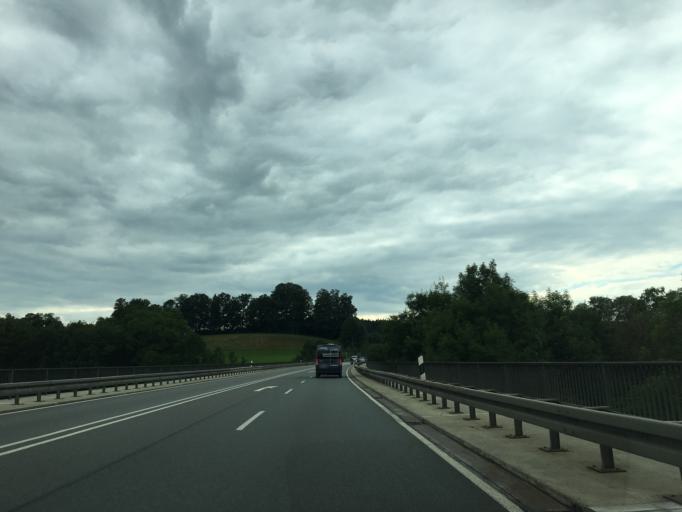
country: DE
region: Bavaria
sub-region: Upper Bavaria
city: Miesbach
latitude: 47.7807
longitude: 11.8284
